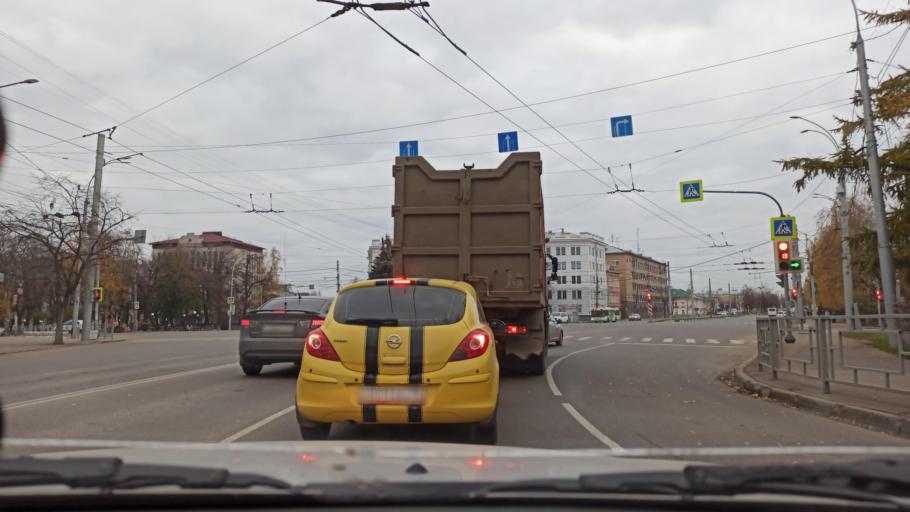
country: RU
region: Vologda
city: Vologda
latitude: 59.2174
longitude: 39.8830
